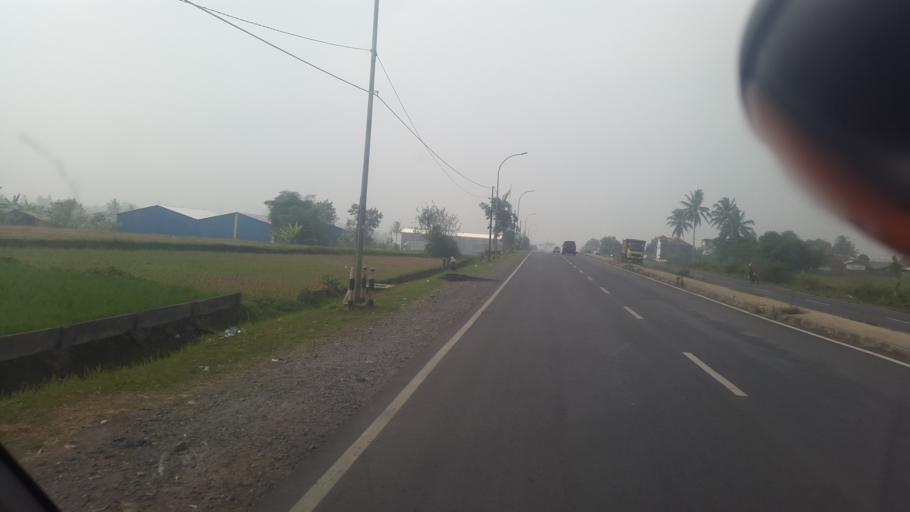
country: ID
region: West Java
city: Sukabumi
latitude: -6.9190
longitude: 106.8874
